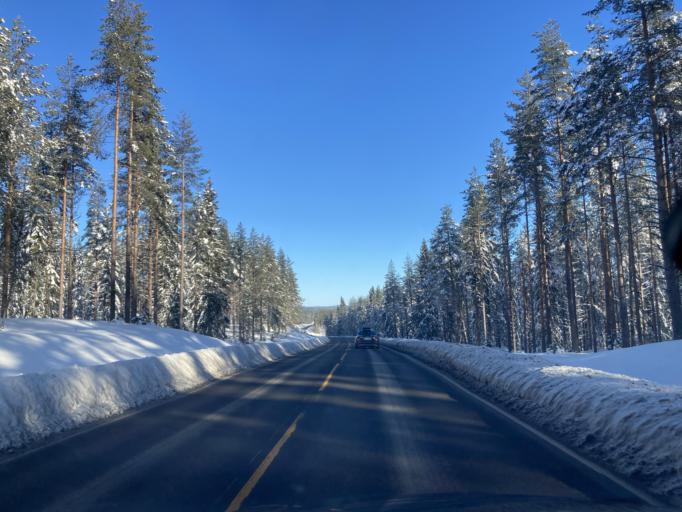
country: NO
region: Hedmark
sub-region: Trysil
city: Innbygda
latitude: 61.1794
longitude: 12.1850
